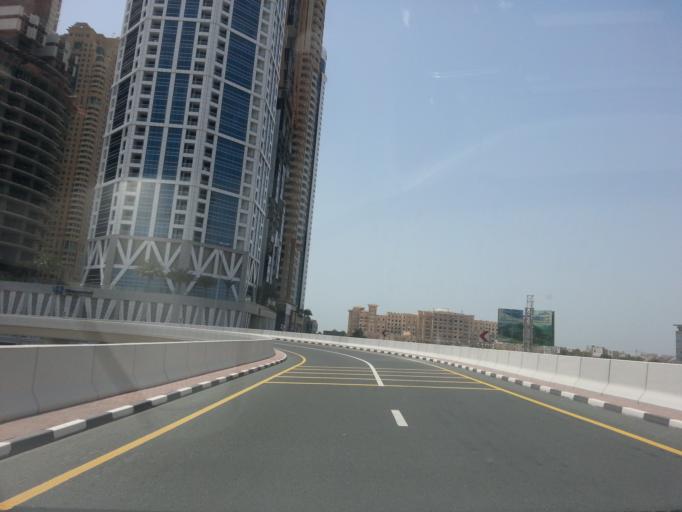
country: AE
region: Dubai
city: Dubai
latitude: 25.0892
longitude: 55.1522
